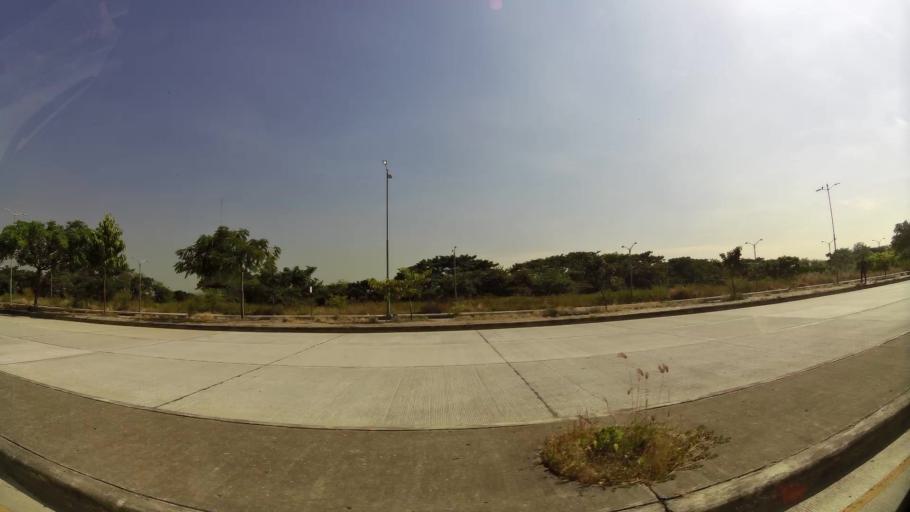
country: EC
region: Guayas
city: Eloy Alfaro
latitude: -2.0999
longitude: -79.8963
